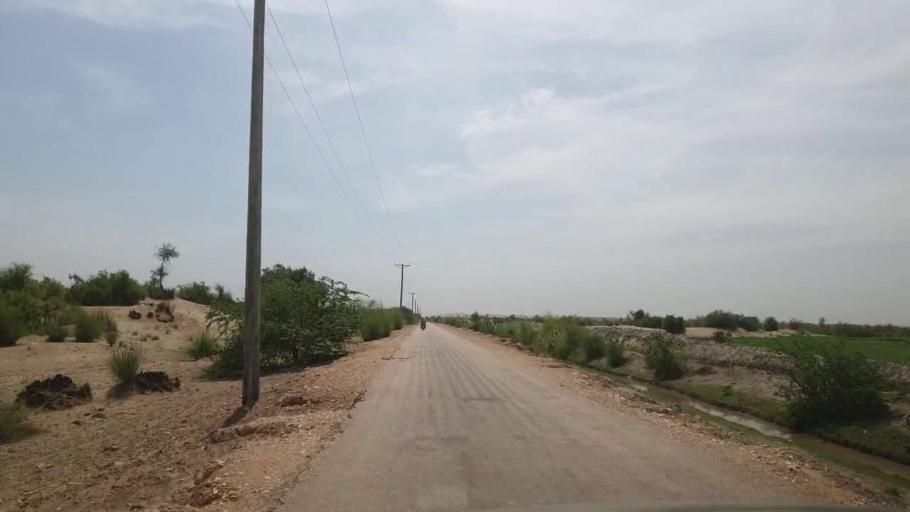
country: PK
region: Sindh
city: Kot Diji
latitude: 27.1170
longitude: 69.0091
